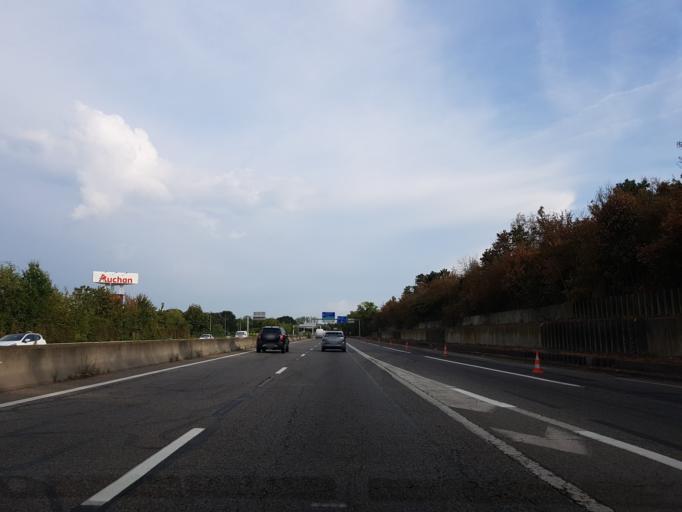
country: FR
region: Alsace
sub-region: Departement du Haut-Rhin
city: Illzach
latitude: 47.7766
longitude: 7.3345
